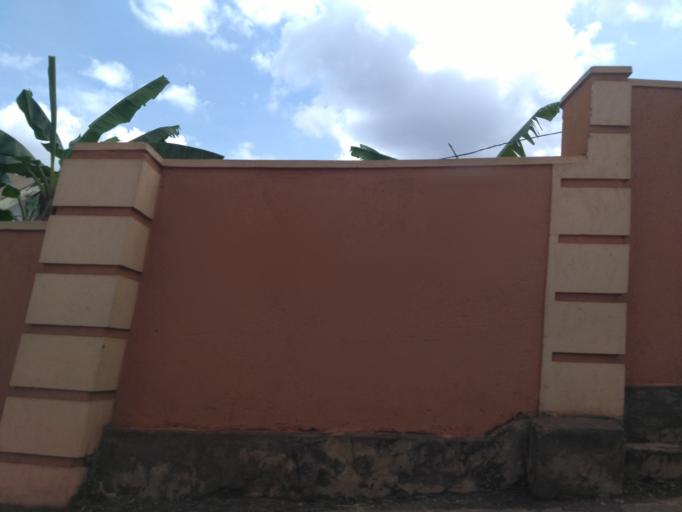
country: UG
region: Central Region
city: Kampala Central Division
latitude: 0.3598
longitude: 32.5837
